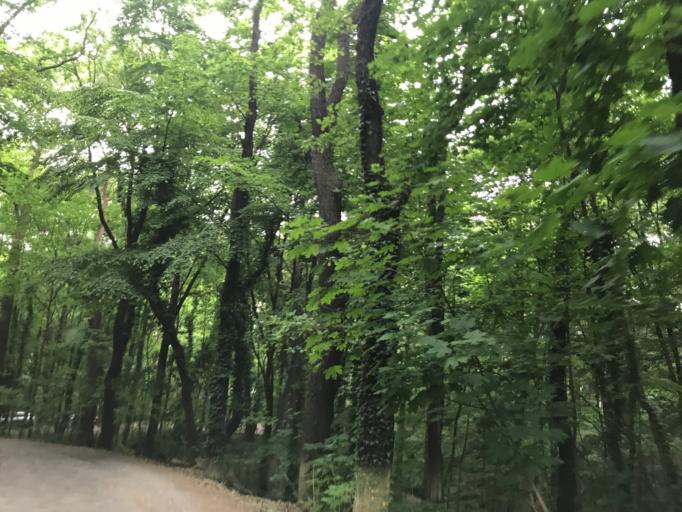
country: DE
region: Berlin
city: Wilhelmstadt
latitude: 52.5086
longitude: 13.2064
